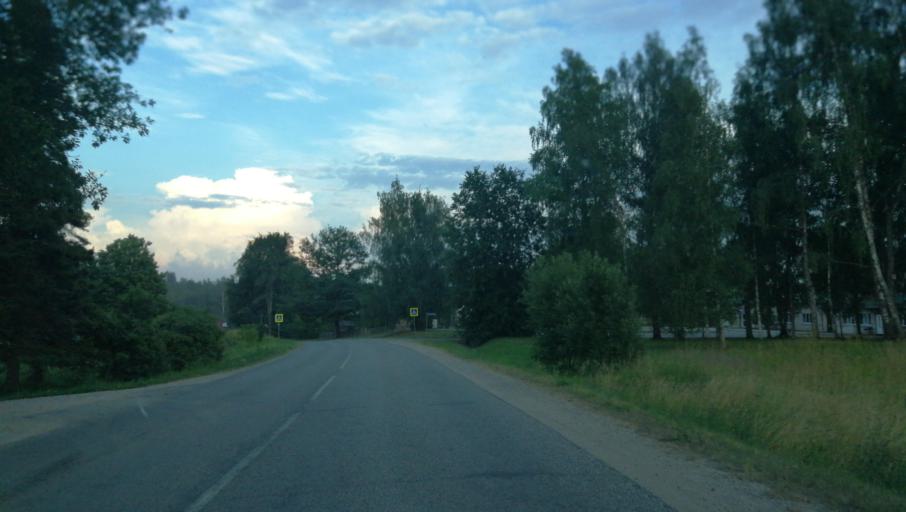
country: LV
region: Priekuli
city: Priekuli
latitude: 57.2754
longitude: 25.3244
